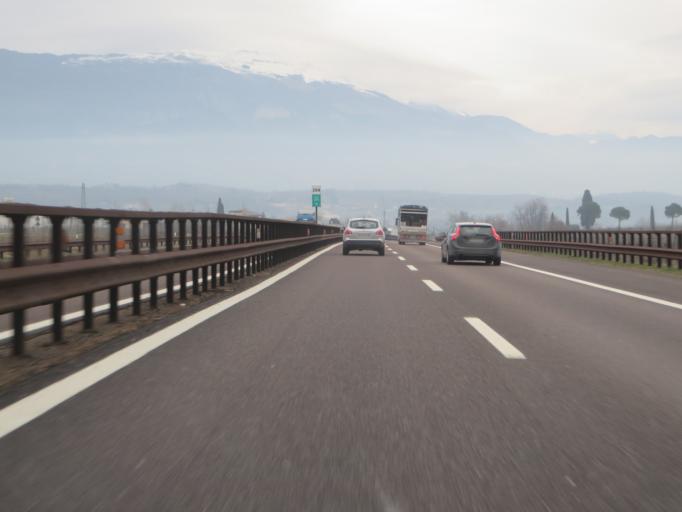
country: IT
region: Veneto
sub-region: Provincia di Verona
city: Rivoli Veronese
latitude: 45.5688
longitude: 10.8031
